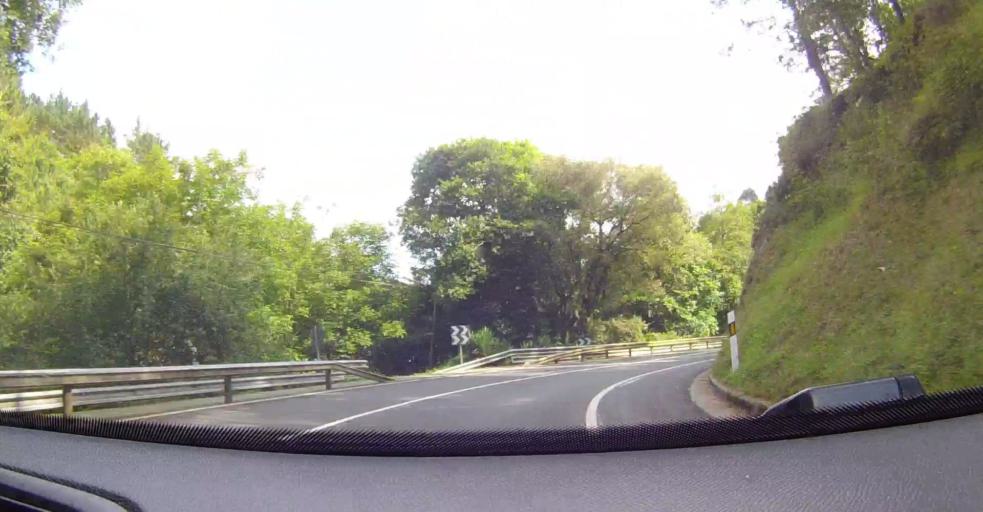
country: ES
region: Basque Country
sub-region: Bizkaia
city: Elantxobe
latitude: 43.4001
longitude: -2.6470
